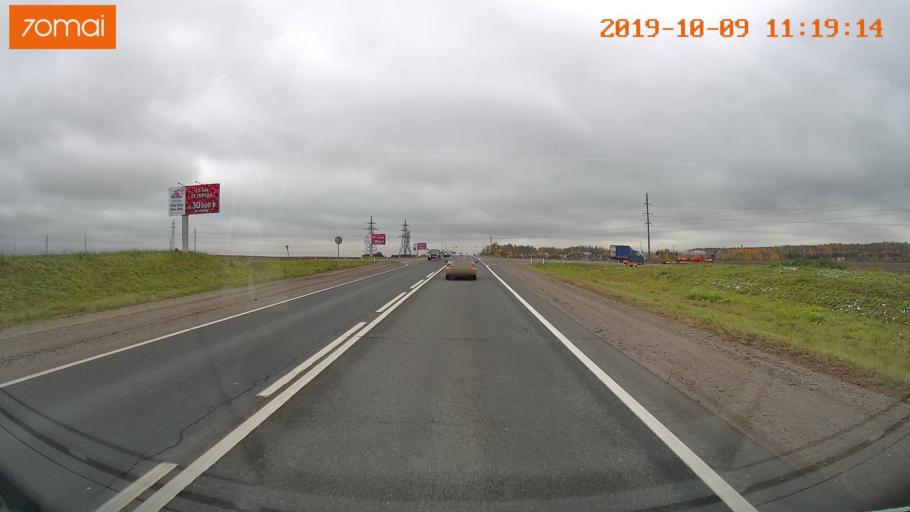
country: RU
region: Vologda
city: Vologda
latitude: 59.1620
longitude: 39.9249
